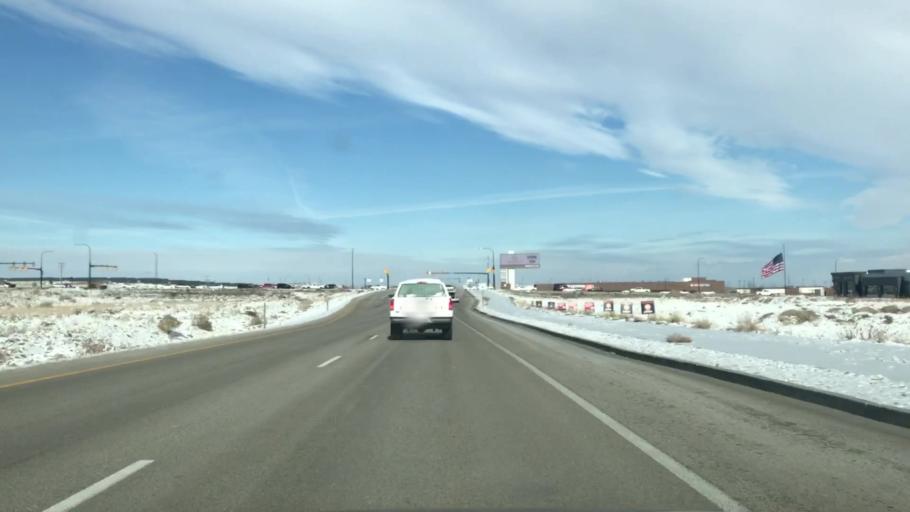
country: US
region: Utah
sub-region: Salt Lake County
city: Herriman
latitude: 40.5055
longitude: -112.0037
